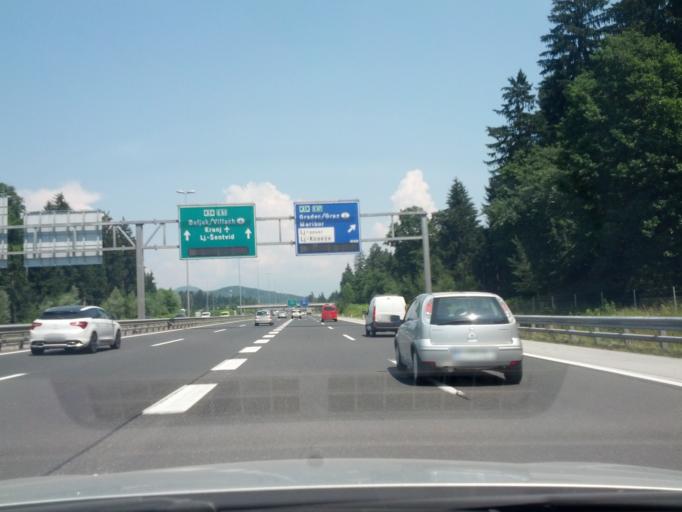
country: SI
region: Ljubljana
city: Ljubljana
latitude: 46.0629
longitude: 14.4559
